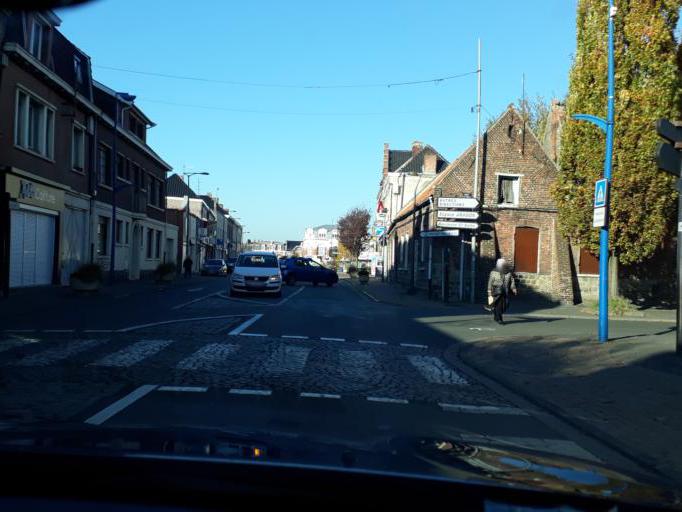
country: FR
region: Nord-Pas-de-Calais
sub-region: Departement du Nord
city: Dechy
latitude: 50.3629
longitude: 3.1146
